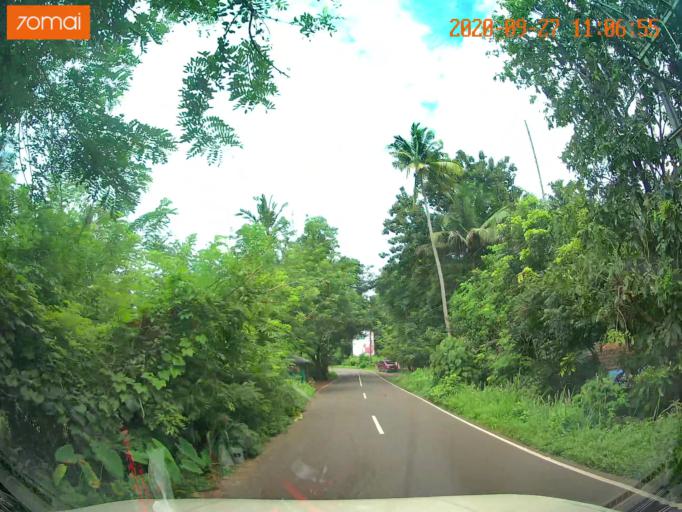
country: IN
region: Kerala
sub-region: Thrissur District
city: Irinjalakuda
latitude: 10.4272
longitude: 76.2393
